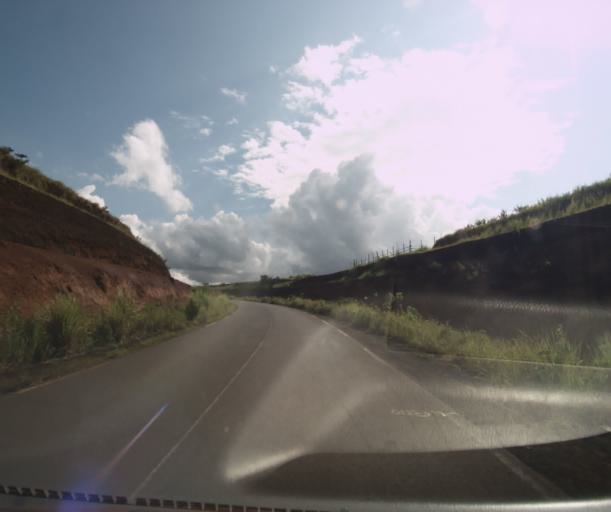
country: CM
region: West
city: Foumban
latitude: 5.7056
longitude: 10.8328
